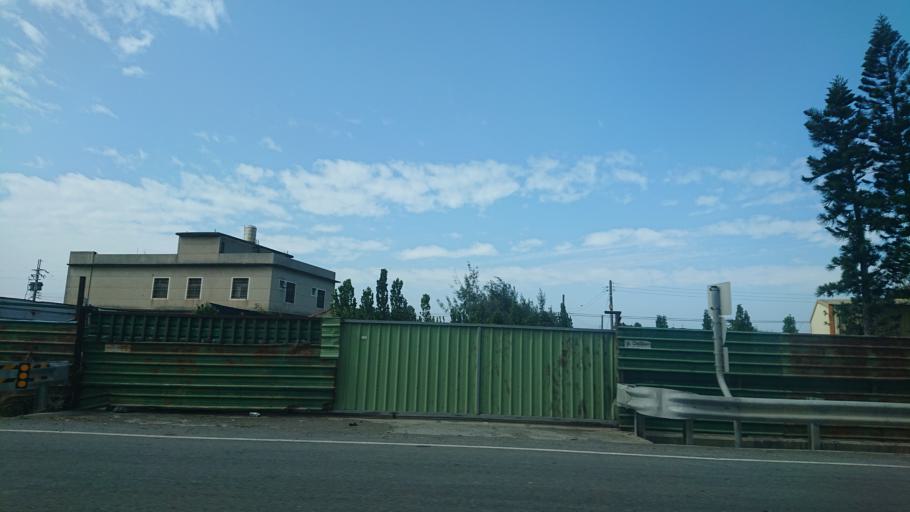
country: TW
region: Taiwan
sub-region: Yunlin
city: Douliu
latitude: 23.8609
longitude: 120.2954
